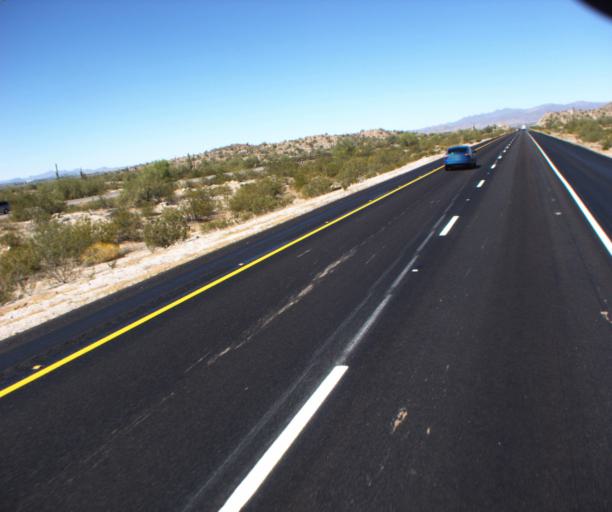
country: US
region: Arizona
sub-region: Maricopa County
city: Buckeye
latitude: 33.2911
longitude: -112.6286
